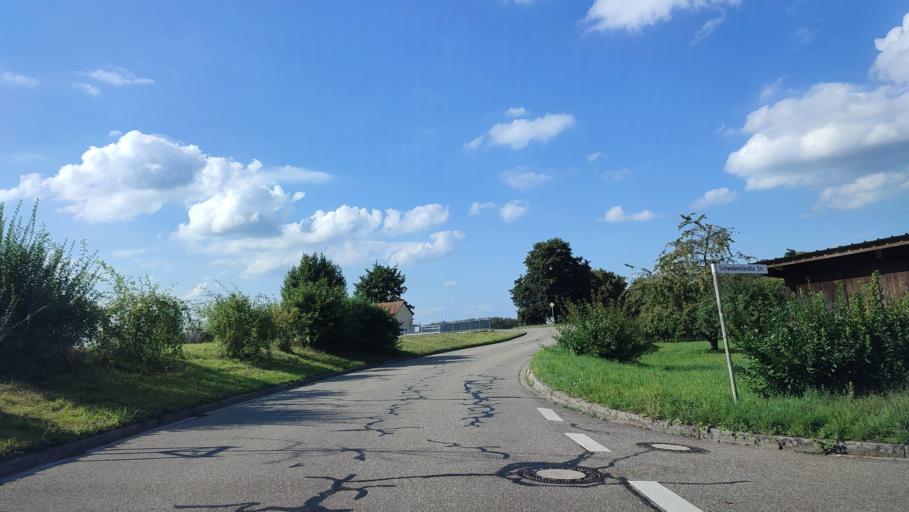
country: DE
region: Baden-Wuerttemberg
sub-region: Freiburg Region
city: Renchen
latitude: 48.5704
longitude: 8.0200
